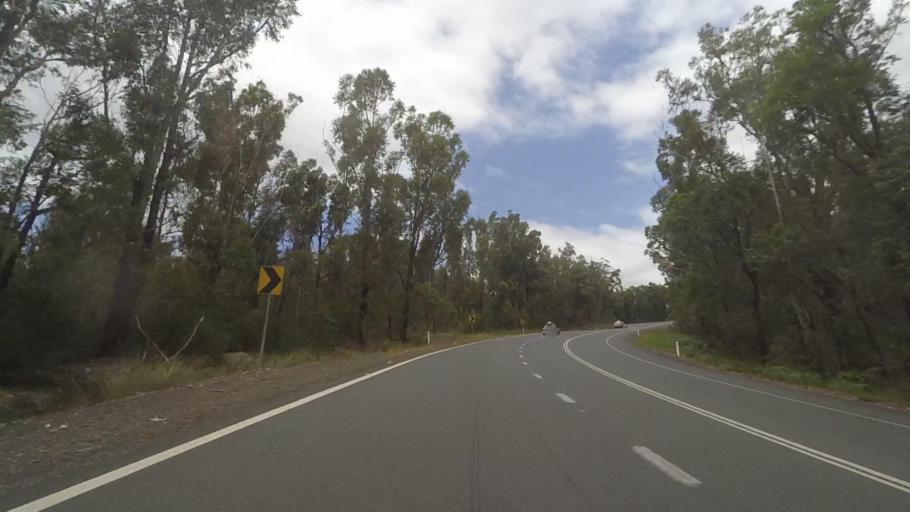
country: AU
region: New South Wales
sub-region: Shoalhaven Shire
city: Milton
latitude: -35.1385
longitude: 150.4651
